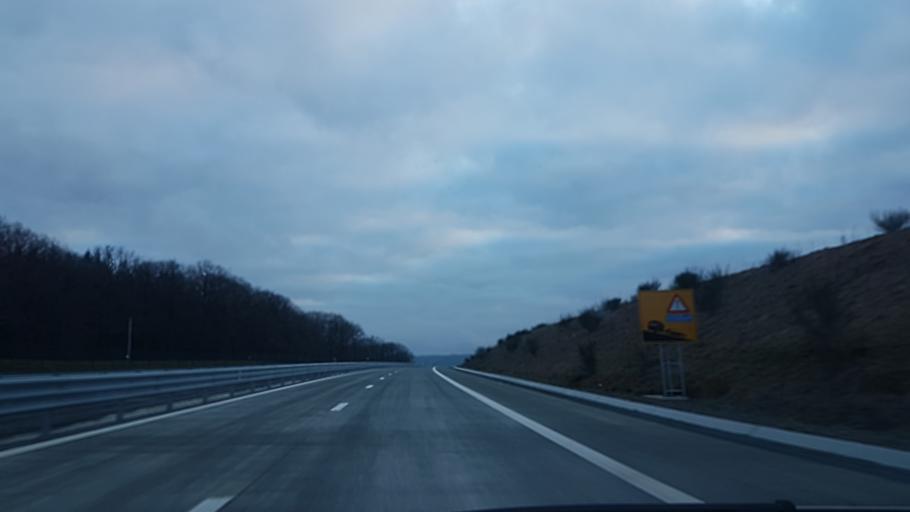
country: FR
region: Champagne-Ardenne
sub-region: Departement des Ardennes
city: Rocroi
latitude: 49.9935
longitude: 4.5429
